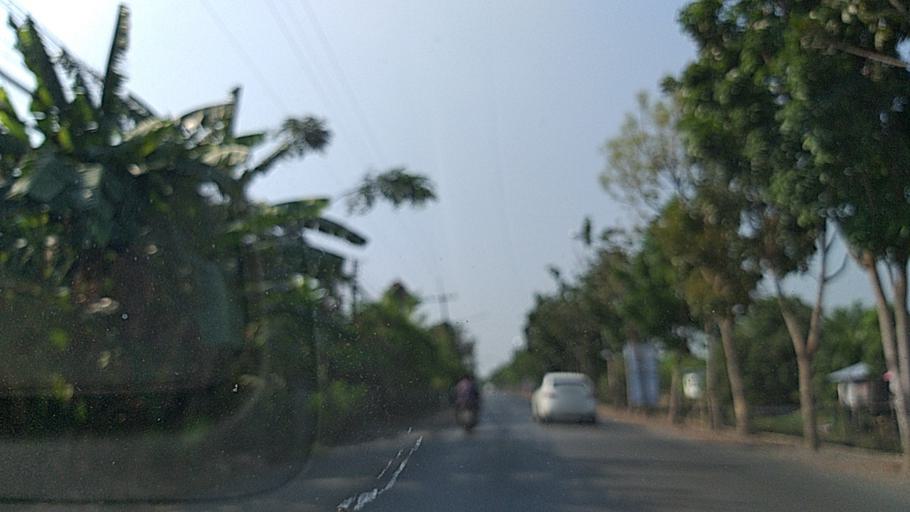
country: TH
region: Pathum Thani
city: Lam Luk Ka
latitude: 13.9563
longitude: 100.7057
